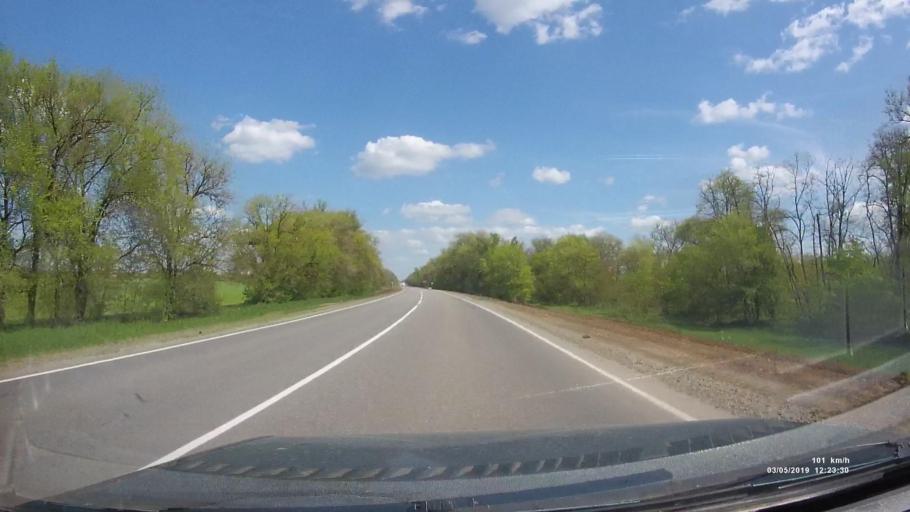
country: RU
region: Rostov
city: Semikarakorsk
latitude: 47.4099
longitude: 40.6844
